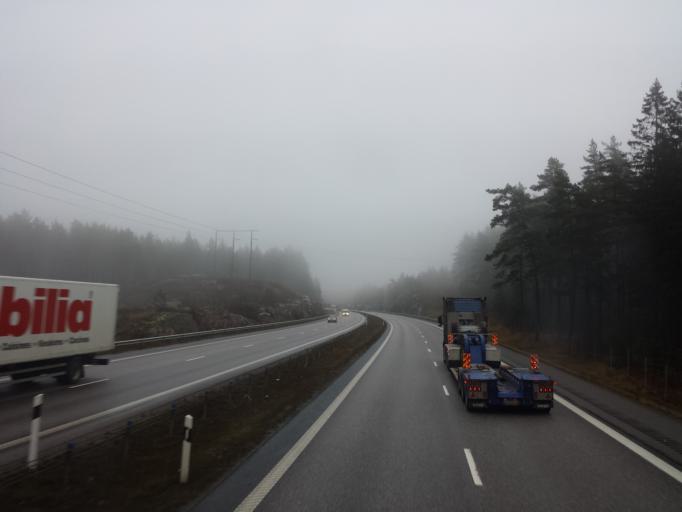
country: SE
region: OEstergoetland
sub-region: Norrkopings Kommun
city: Krokek
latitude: 58.6800
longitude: 16.3160
